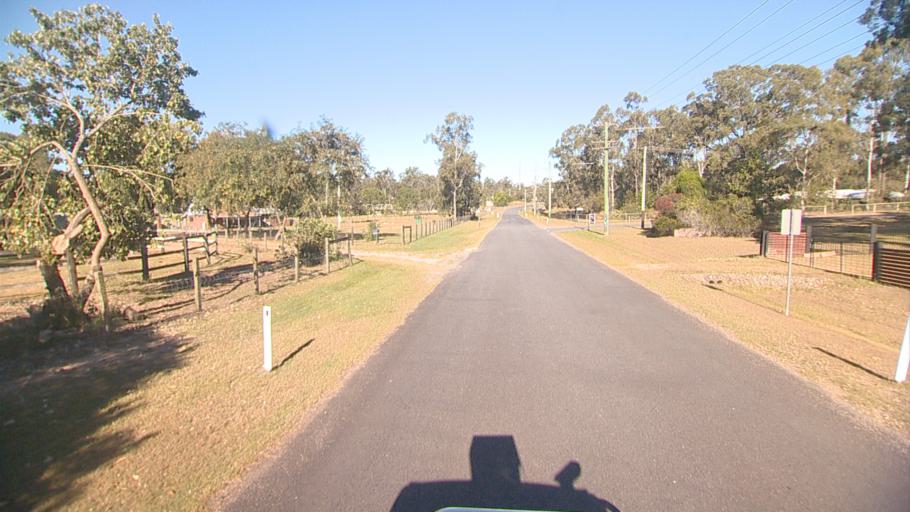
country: AU
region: Queensland
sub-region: Logan
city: Park Ridge South
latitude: -27.7299
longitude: 153.0205
